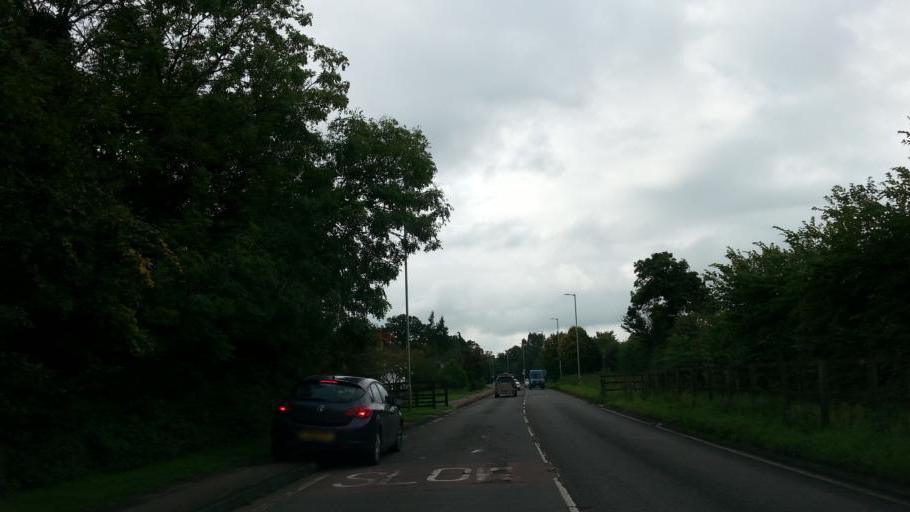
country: GB
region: England
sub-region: Hertfordshire
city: Hitchin
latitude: 51.9708
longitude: -0.2878
